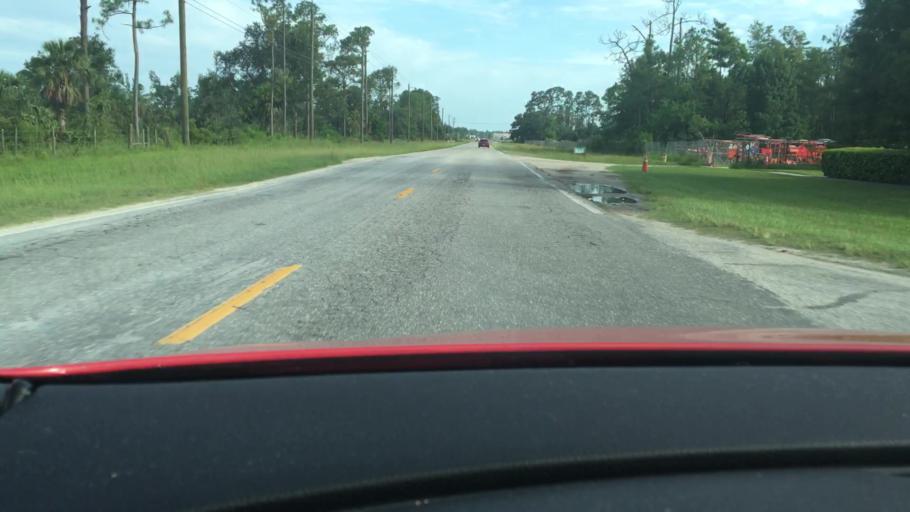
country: US
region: Florida
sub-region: Volusia County
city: Daytona Beach
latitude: 29.1804
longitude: -81.0917
